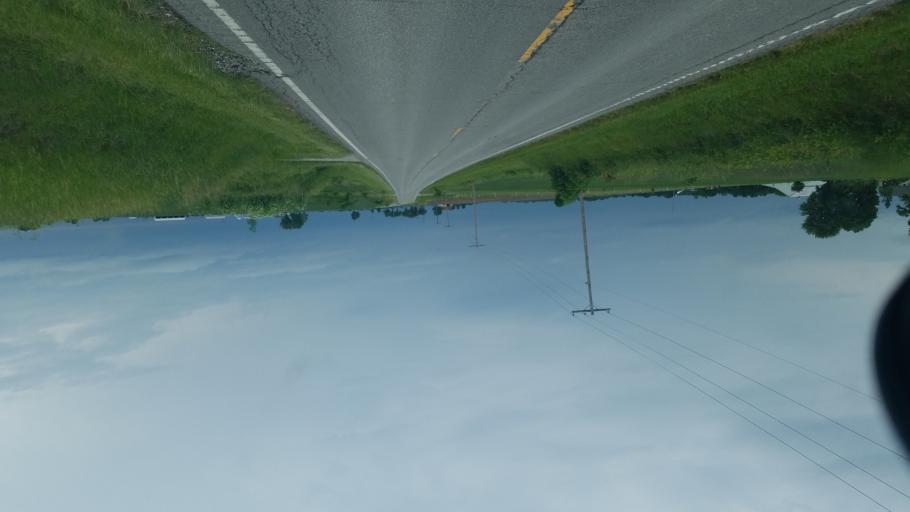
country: US
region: Missouri
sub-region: Cooper County
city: Boonville
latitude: 38.8484
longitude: -92.6316
